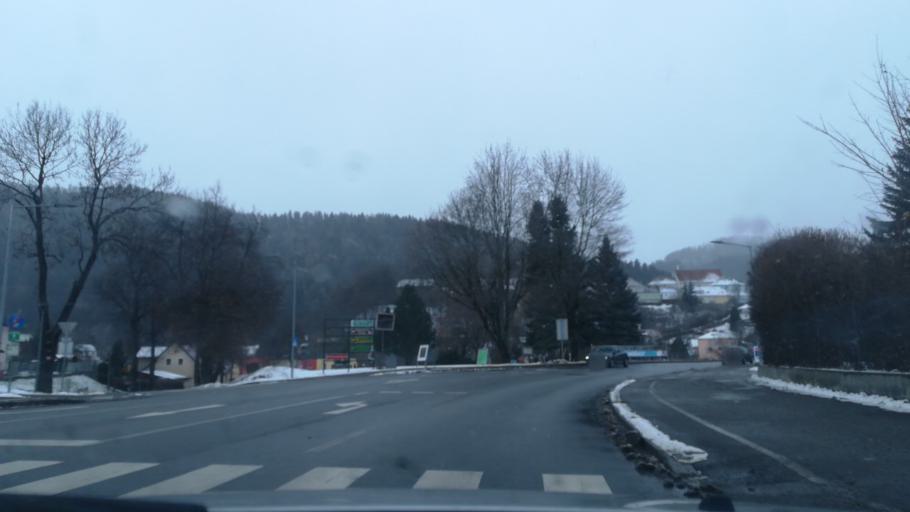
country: AT
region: Styria
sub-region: Politischer Bezirk Murtal
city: Judenburg
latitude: 47.1730
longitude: 14.6664
